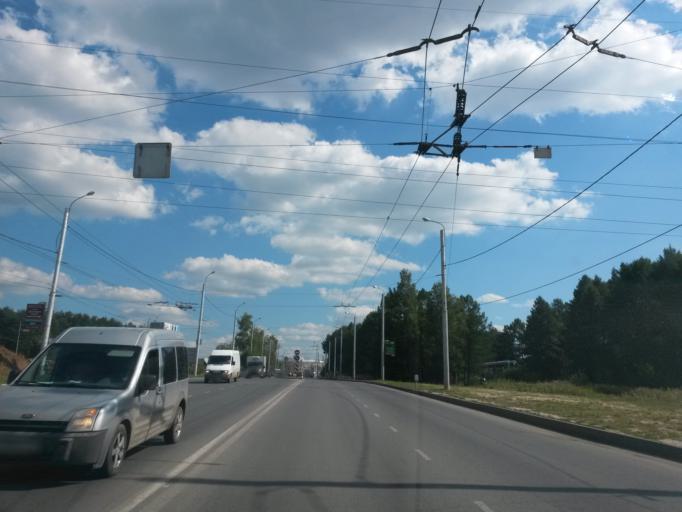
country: RU
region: Ivanovo
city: Kokhma
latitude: 56.9605
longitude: 41.0305
